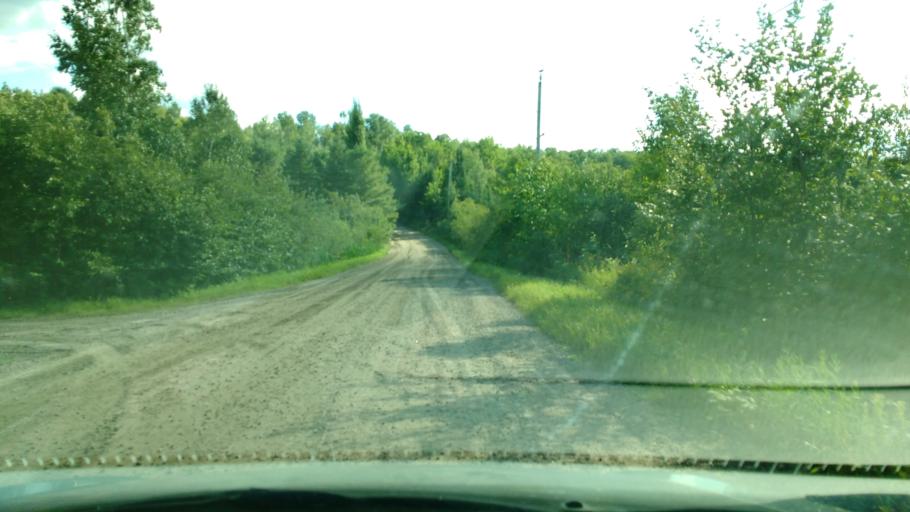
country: CA
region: Ontario
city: Powassan
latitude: 46.1893
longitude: -79.2808
